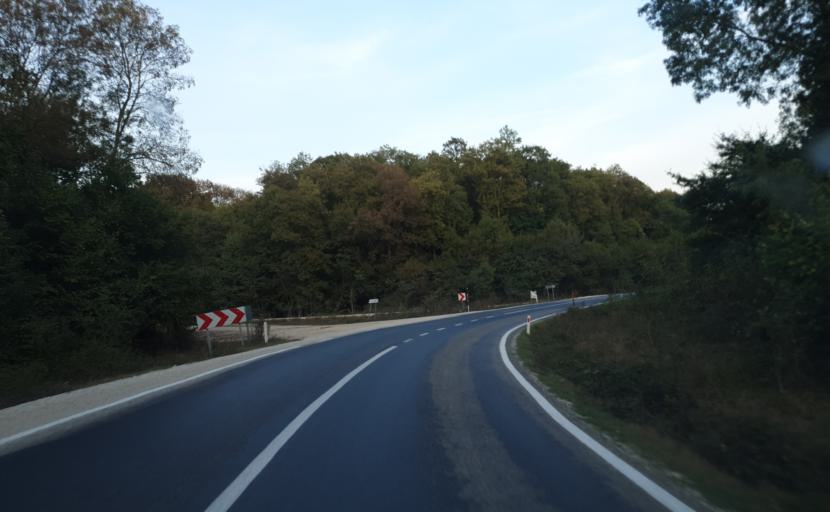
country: TR
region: Kirklareli
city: Igneada
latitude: 41.8753
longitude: 27.9176
